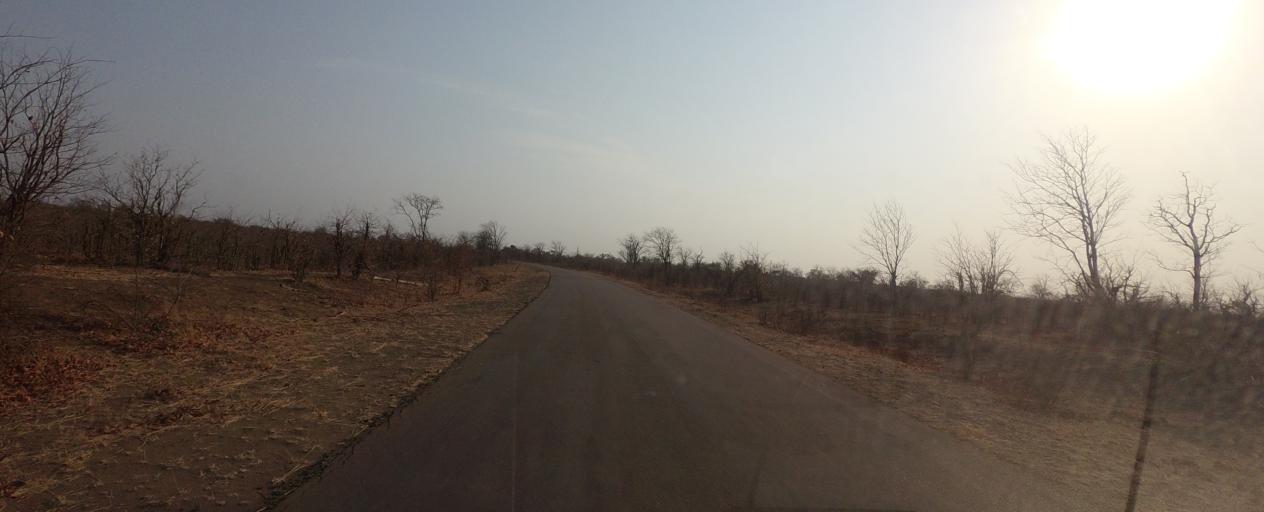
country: ZA
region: Limpopo
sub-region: Mopani District Municipality
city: Giyani
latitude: -23.0920
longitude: 31.4203
